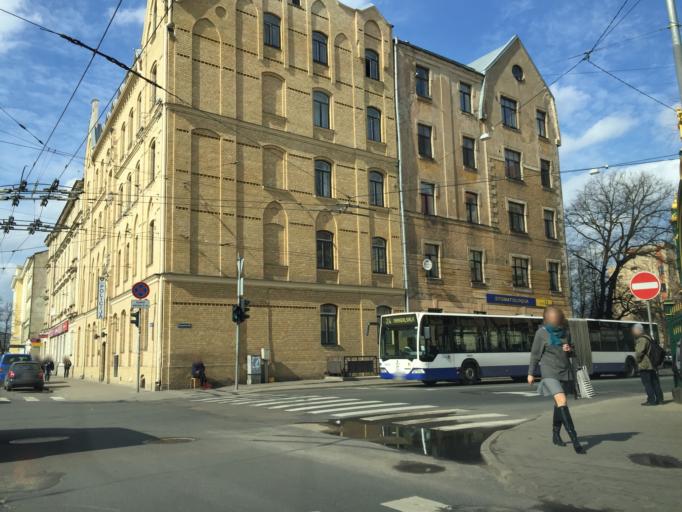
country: LV
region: Riga
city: Riga
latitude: 56.9439
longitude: 24.1225
